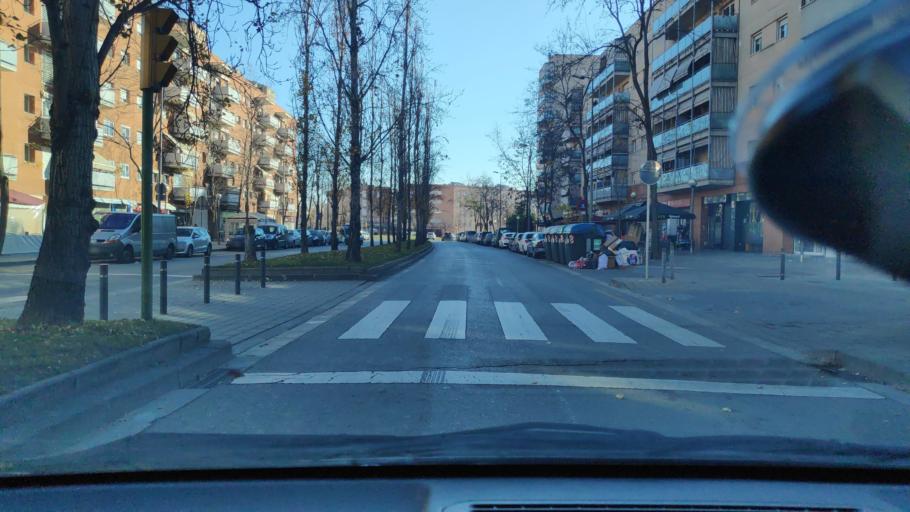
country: ES
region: Catalonia
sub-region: Provincia de Barcelona
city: Sant Quirze del Valles
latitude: 41.5602
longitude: 2.0824
